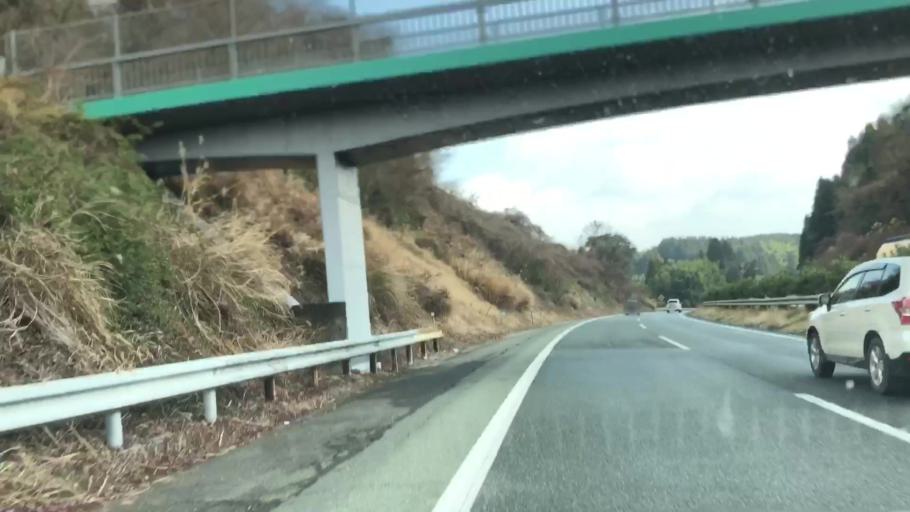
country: JP
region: Fukuoka
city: Omuta
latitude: 33.0429
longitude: 130.5665
